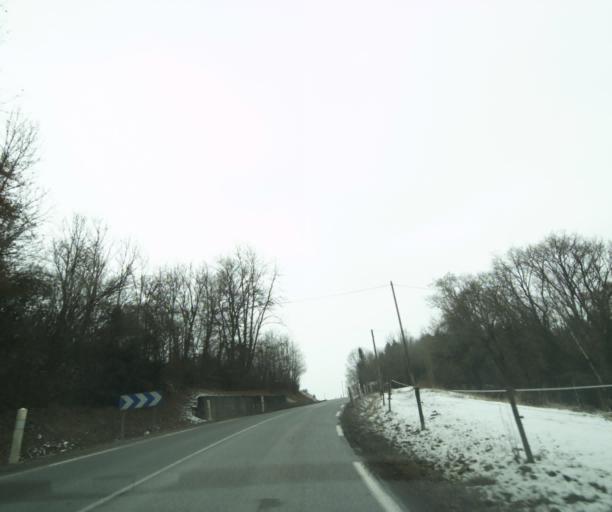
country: FR
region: Rhone-Alpes
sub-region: Departement de la Haute-Savoie
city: Contamine-sur-Arve
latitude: 46.1331
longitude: 6.3127
